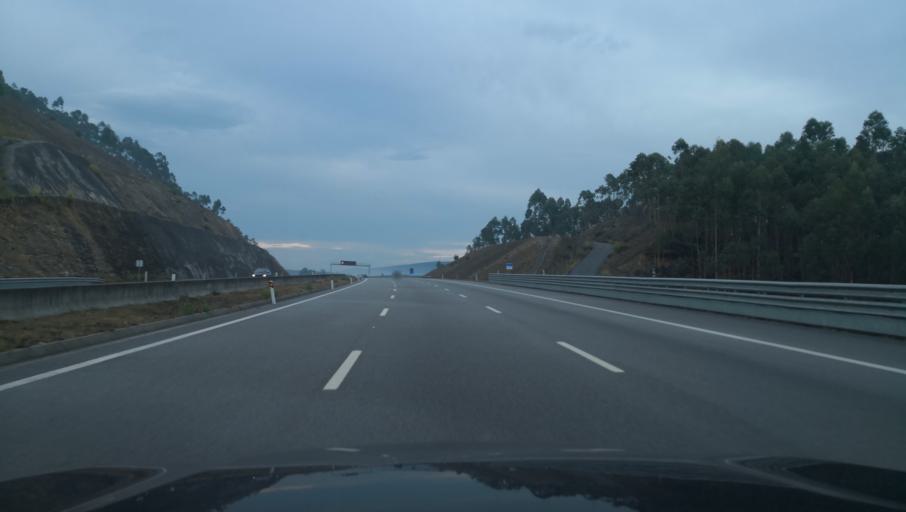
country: PT
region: Porto
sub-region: Paredes
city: Recarei
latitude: 41.1213
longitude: -8.4335
